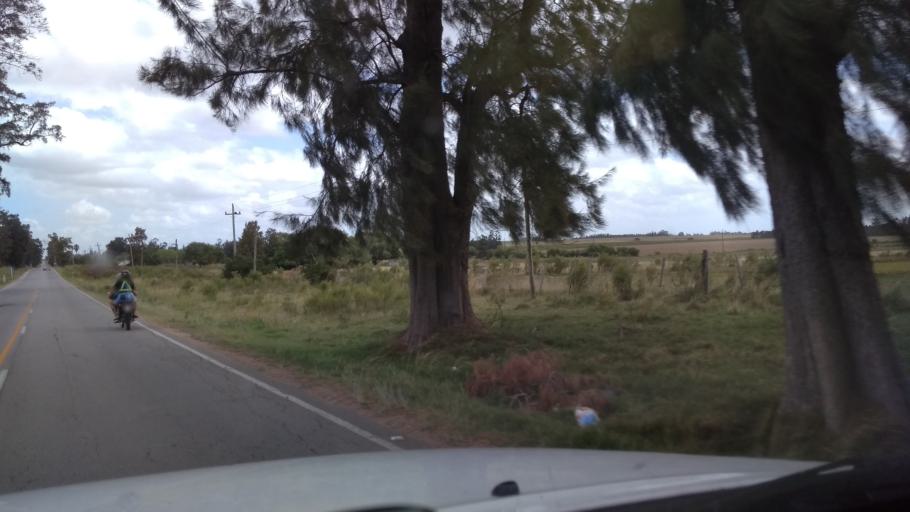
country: UY
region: Canelones
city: San Bautista
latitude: -34.4052
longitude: -55.9598
